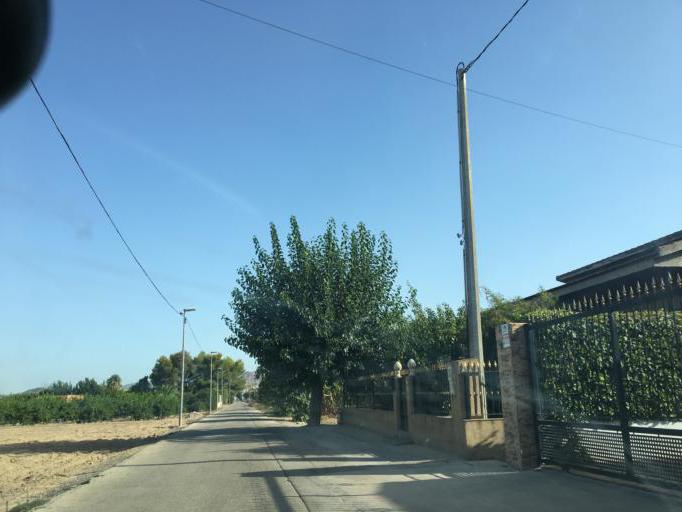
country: ES
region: Murcia
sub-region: Murcia
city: Santomera
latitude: 38.0254
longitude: -1.0530
